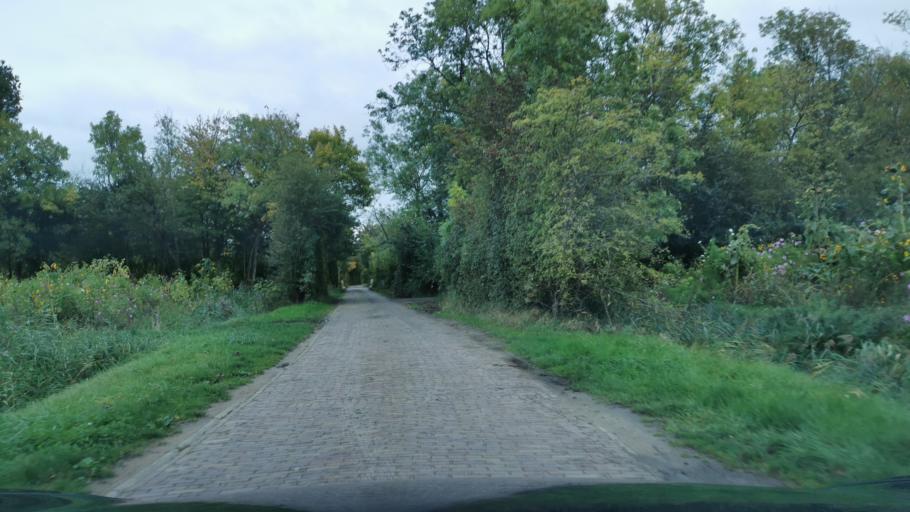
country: NL
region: Zeeland
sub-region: Gemeente Veere
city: Veere
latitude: 51.5549
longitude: 3.6483
